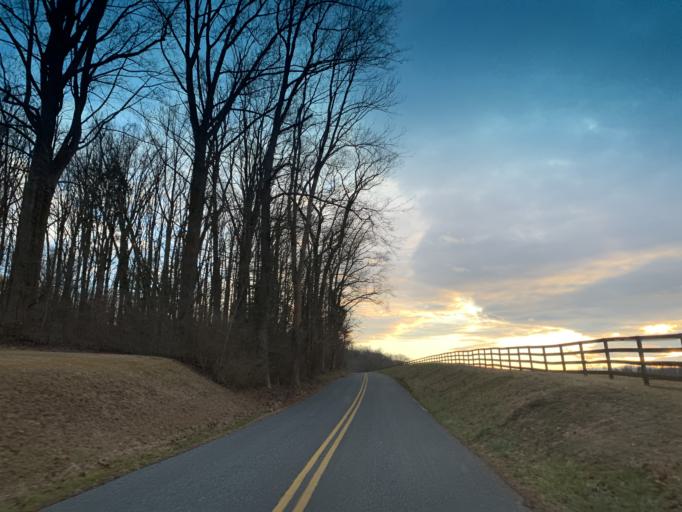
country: US
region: Maryland
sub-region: Harford County
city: Bel Air North
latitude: 39.6090
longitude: -76.3196
